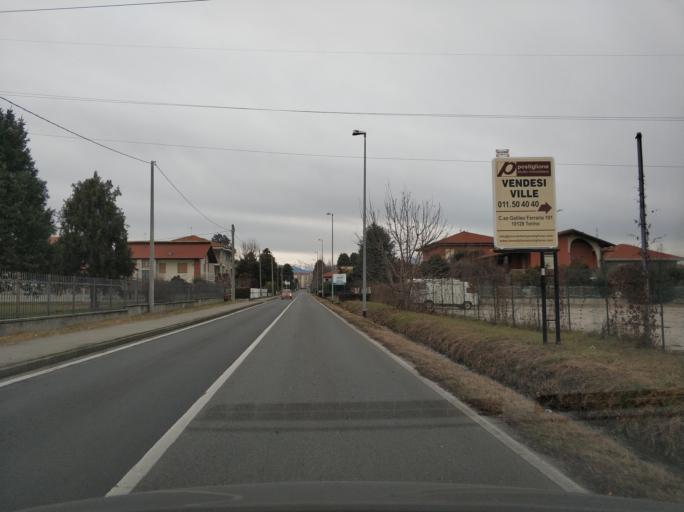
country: IT
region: Piedmont
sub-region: Provincia di Torino
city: San Maurizio
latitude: 45.2096
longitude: 7.6352
